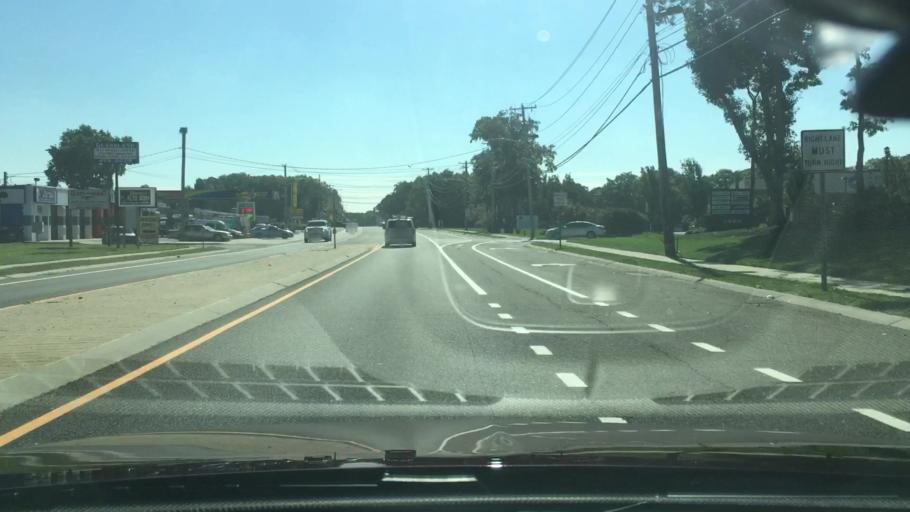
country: US
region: New York
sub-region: Suffolk County
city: Port Jefferson Station
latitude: 40.9113
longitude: -73.0300
